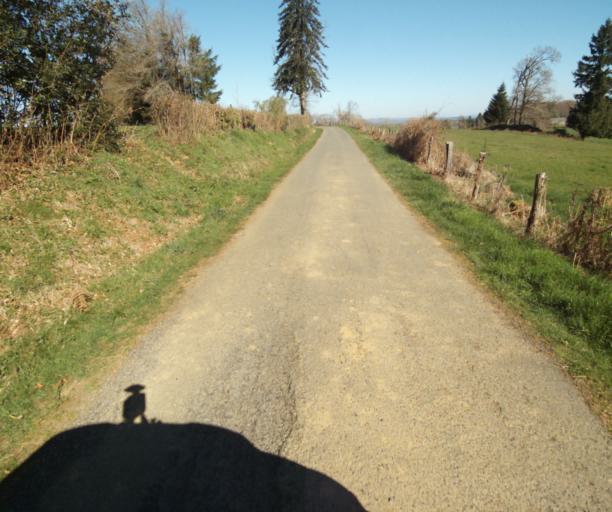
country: FR
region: Limousin
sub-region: Departement de la Correze
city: Chamboulive
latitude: 45.4115
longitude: 1.6908
